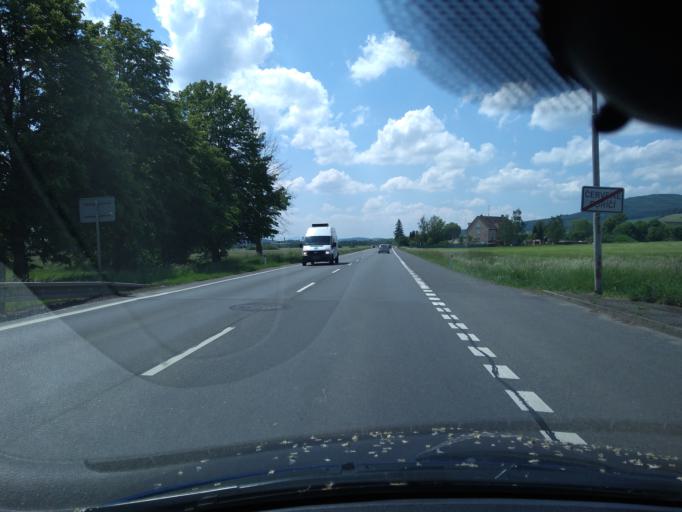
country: CZ
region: Plzensky
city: Svihov
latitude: 49.4984
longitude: 13.2921
